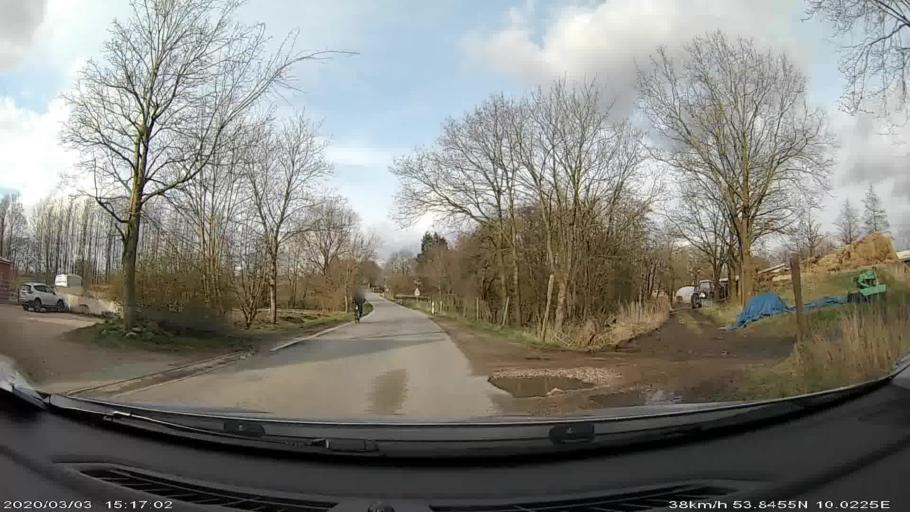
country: DE
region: Schleswig-Holstein
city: Kattendorf
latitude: 53.8452
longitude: 10.0225
